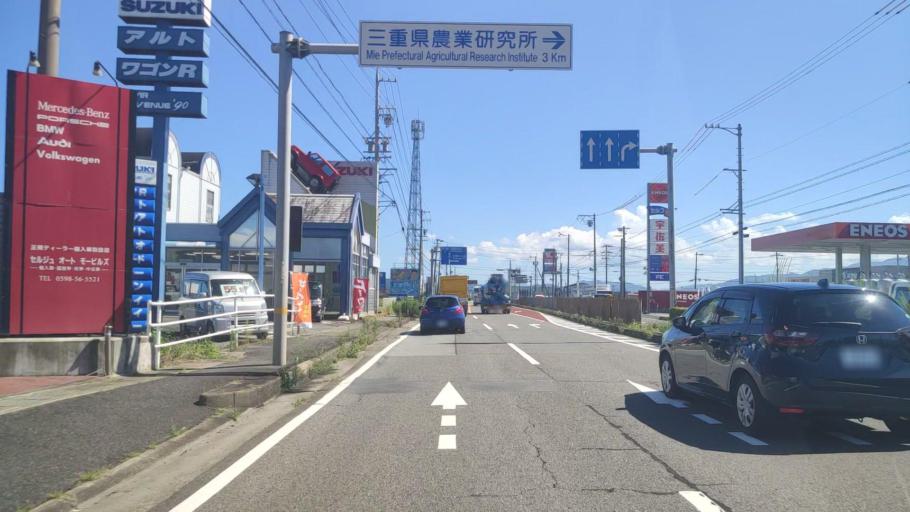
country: JP
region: Mie
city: Hisai-motomachi
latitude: 34.6364
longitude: 136.5177
